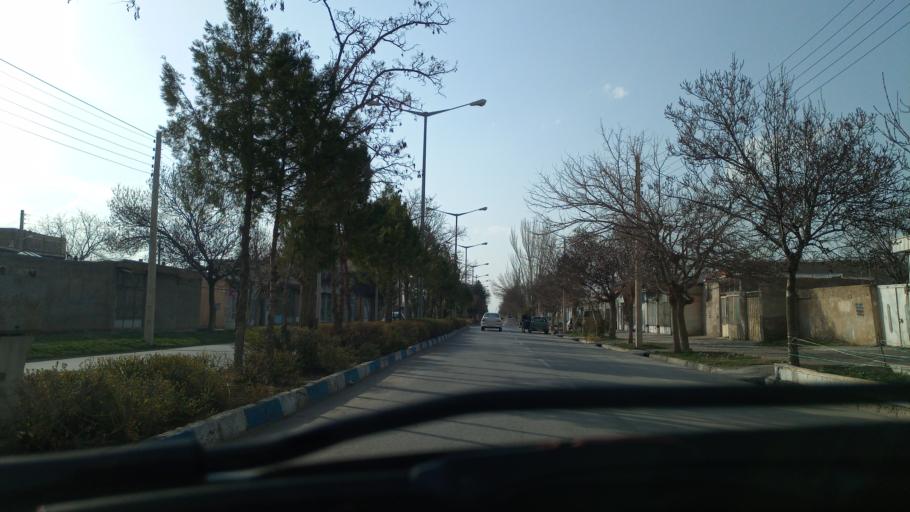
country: IR
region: Razavi Khorasan
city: Quchan
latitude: 37.1005
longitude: 58.5000
